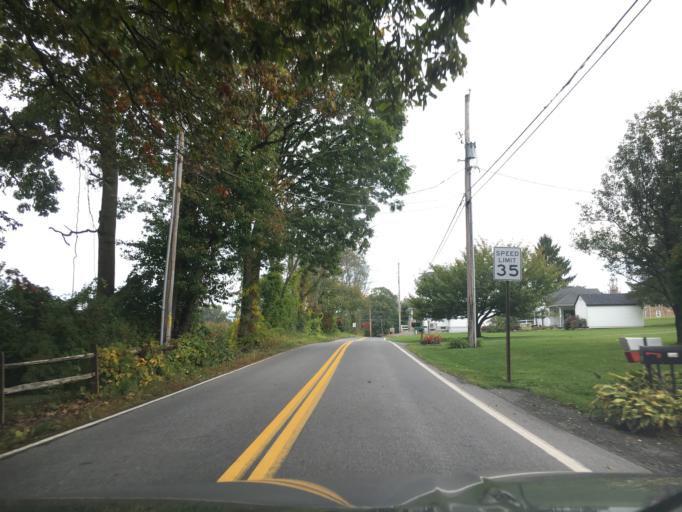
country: US
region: Pennsylvania
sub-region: Berks County
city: Fleetwood
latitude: 40.4547
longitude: -75.7497
